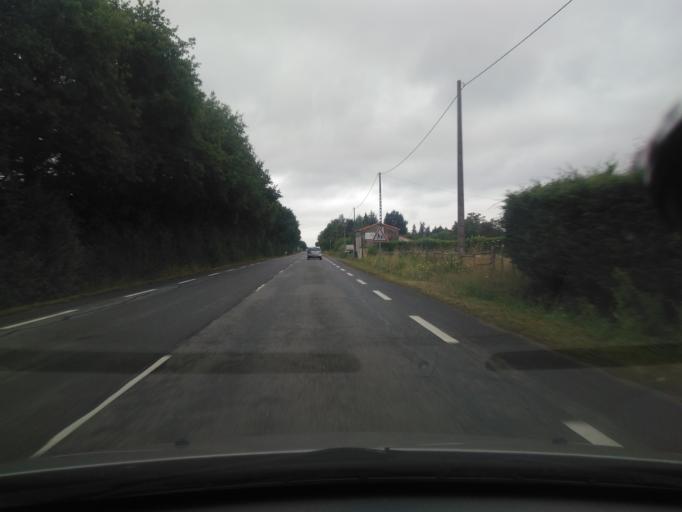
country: FR
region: Pays de la Loire
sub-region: Departement de la Vendee
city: Saint-Florent-des-Bois
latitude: 46.6068
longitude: -1.3394
